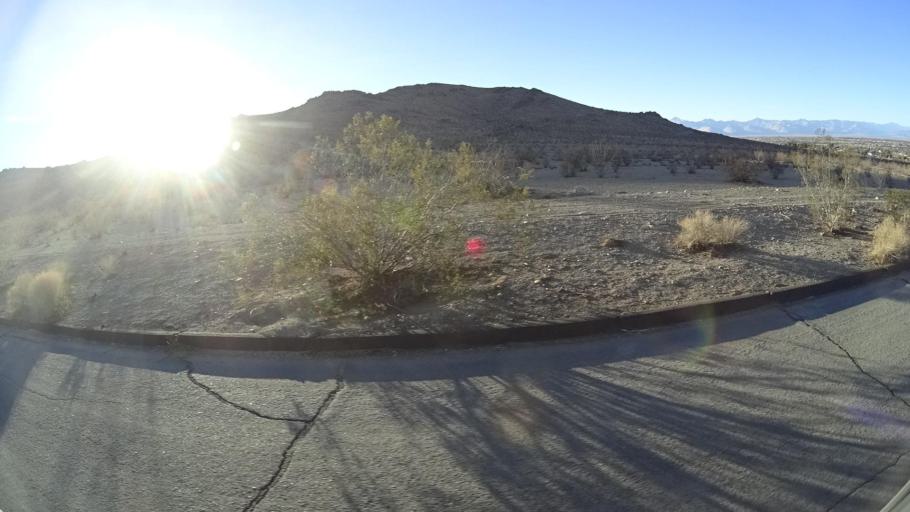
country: US
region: California
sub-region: Kern County
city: Ridgecrest
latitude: 35.5742
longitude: -117.6523
